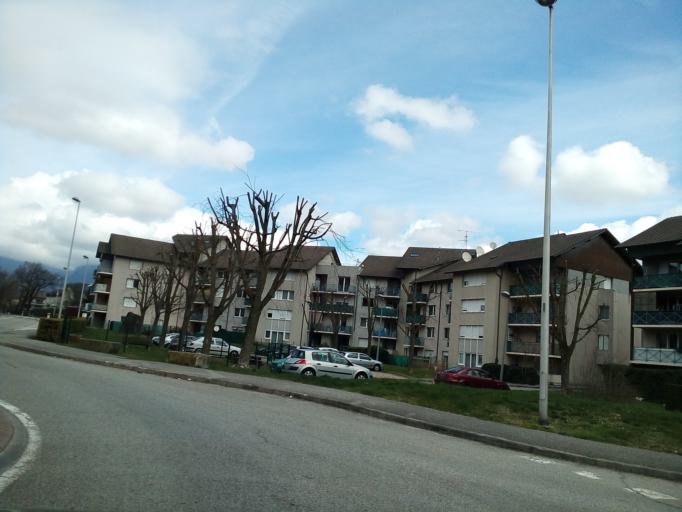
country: FR
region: Rhone-Alpes
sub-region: Departement de la Savoie
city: Saint-Baldoph
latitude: 45.5298
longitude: 5.9557
